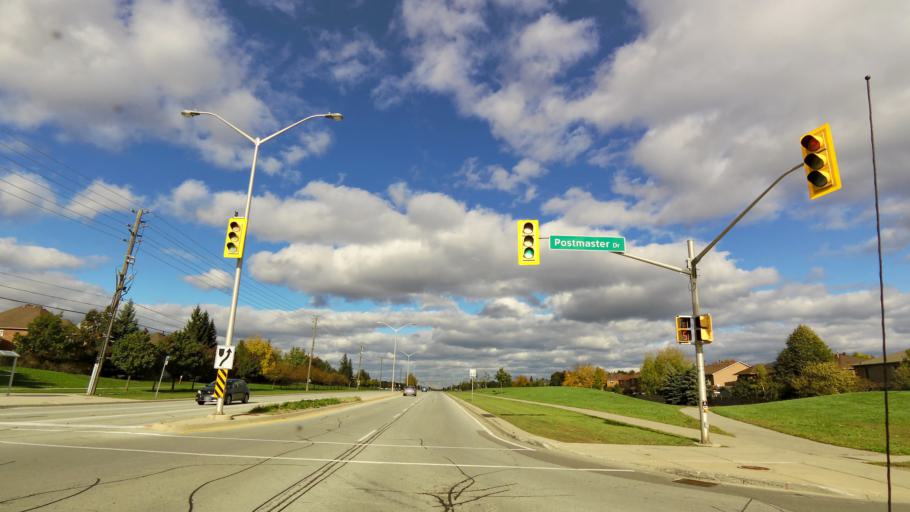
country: CA
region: Ontario
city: Oakville
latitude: 43.4352
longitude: -79.7457
